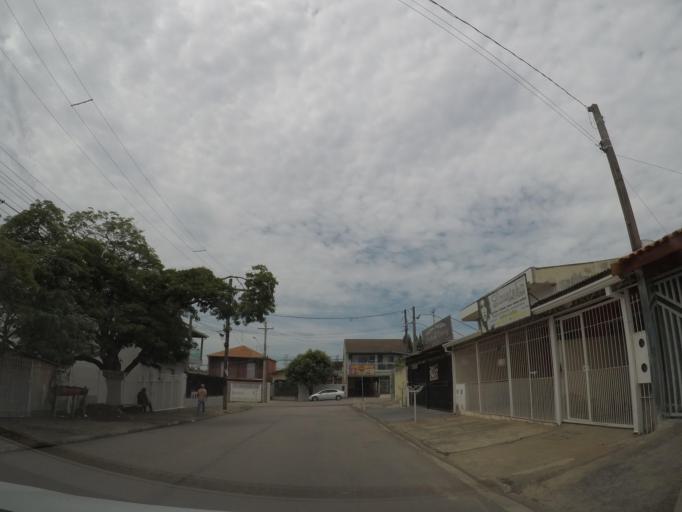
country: BR
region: Sao Paulo
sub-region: Hortolandia
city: Hortolandia
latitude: -22.8424
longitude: -47.1929
